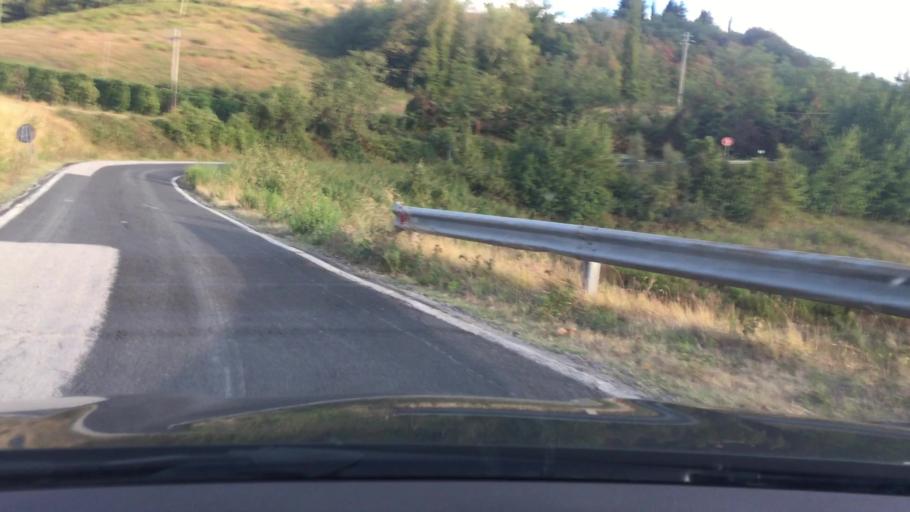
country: IT
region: Emilia-Romagna
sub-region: Provincia di Ravenna
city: Brisighella
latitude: 44.2072
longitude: 11.7776
